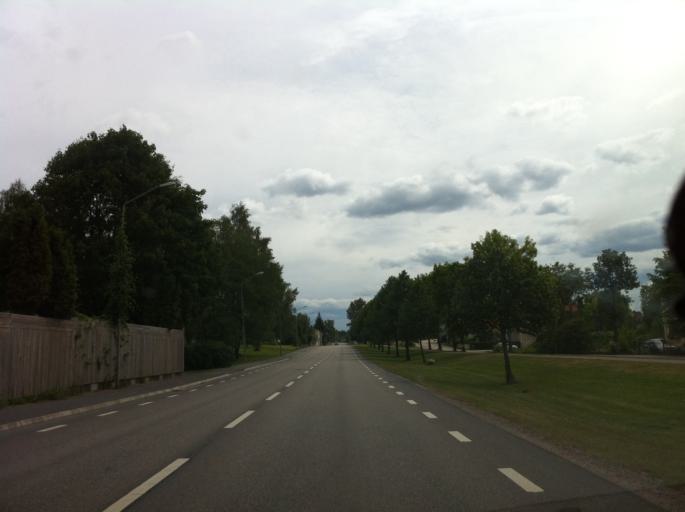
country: SE
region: Blekinge
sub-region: Karlshamns Kommun
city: Svangsta
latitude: 56.4698
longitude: 14.6934
